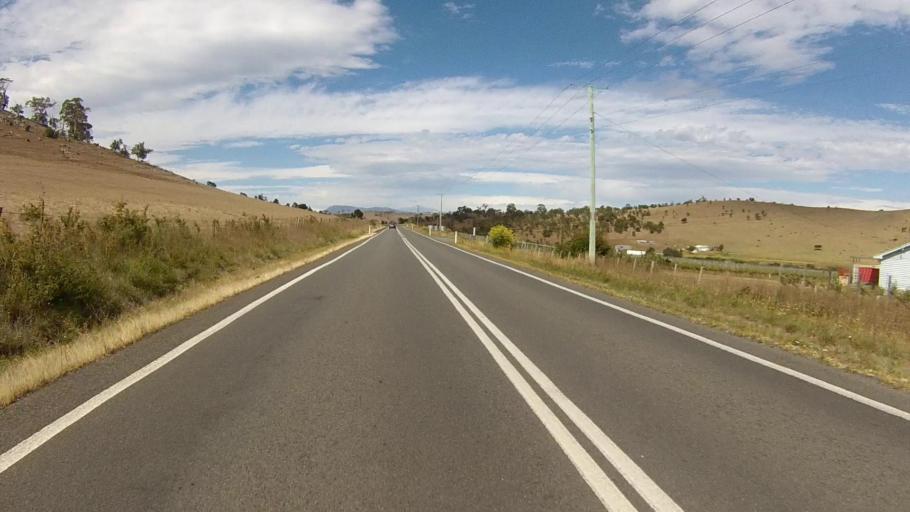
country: AU
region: Tasmania
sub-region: Brighton
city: Old Beach
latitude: -42.6781
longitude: 147.3560
